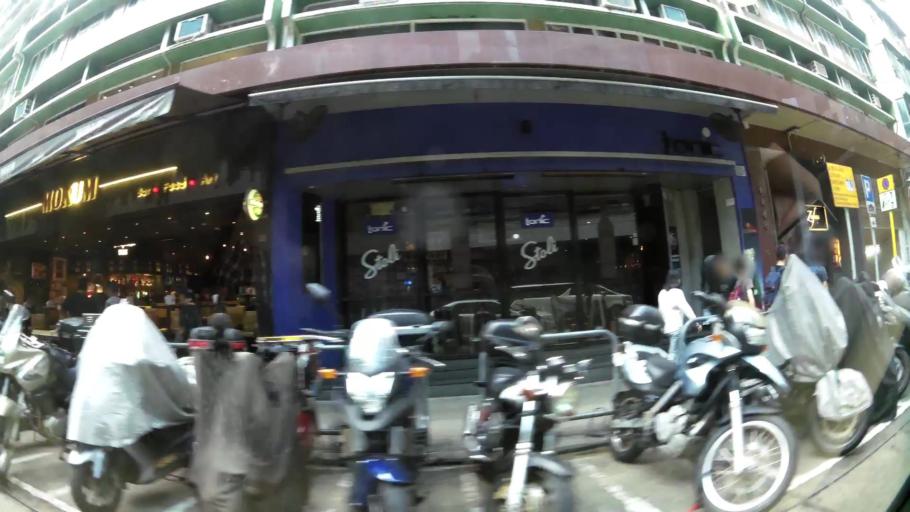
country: HK
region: Central and Western
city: Central
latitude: 22.2809
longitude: 114.1551
